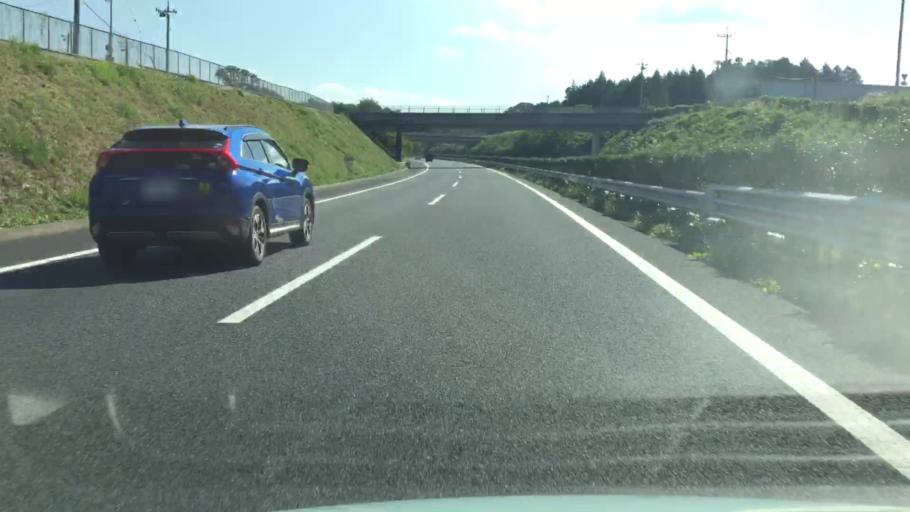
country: JP
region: Ibaraki
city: Tomobe
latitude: 36.3165
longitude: 140.3146
